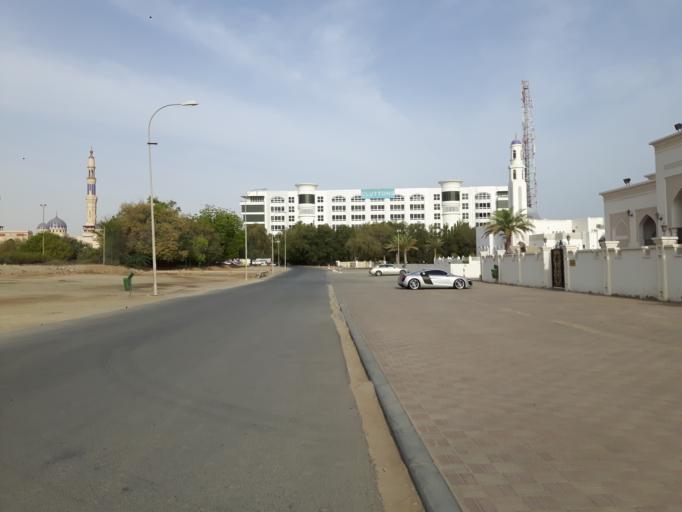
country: OM
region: Muhafazat Masqat
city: Bawshar
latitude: 23.6162
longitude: 58.4799
